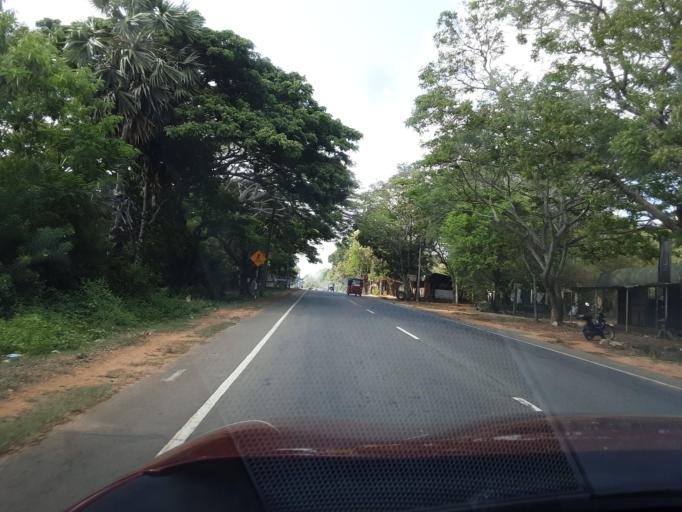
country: LK
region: Southern
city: Tangalla
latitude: 6.2478
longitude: 81.2281
